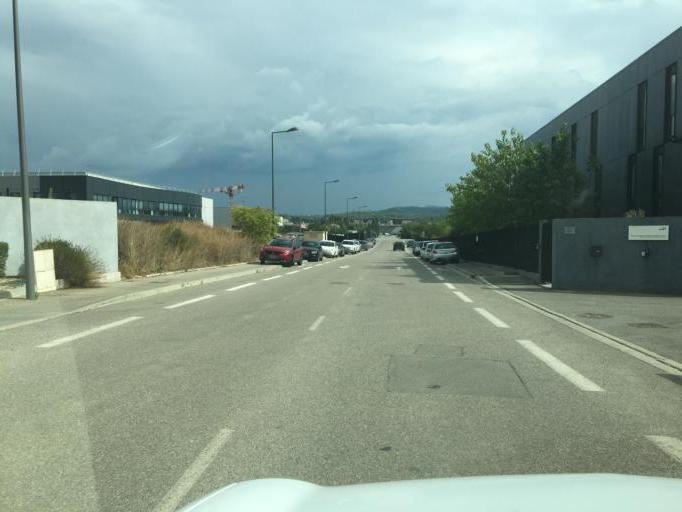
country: FR
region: Provence-Alpes-Cote d'Azur
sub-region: Departement des Bouches-du-Rhone
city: Bouc-Bel-Air
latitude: 43.4843
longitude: 5.3919
